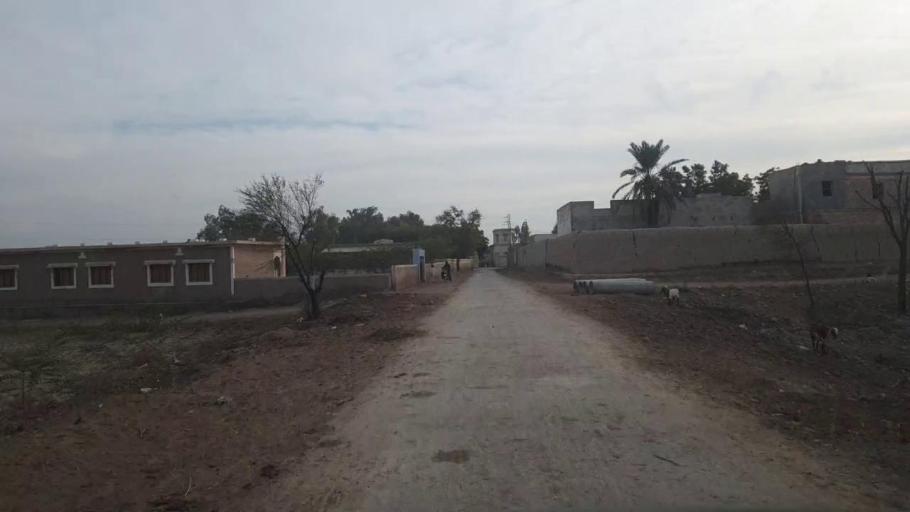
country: PK
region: Sindh
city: Shahpur Chakar
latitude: 26.1330
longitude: 68.6072
